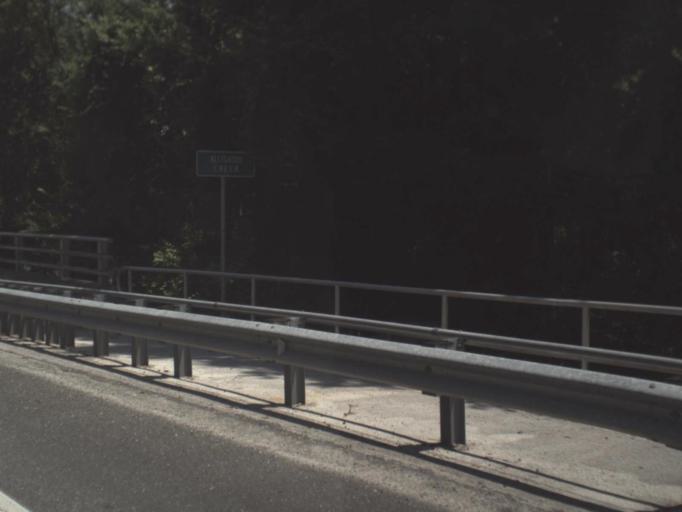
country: US
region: Florida
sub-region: Bradford County
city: Starke
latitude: 29.9378
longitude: -82.1061
